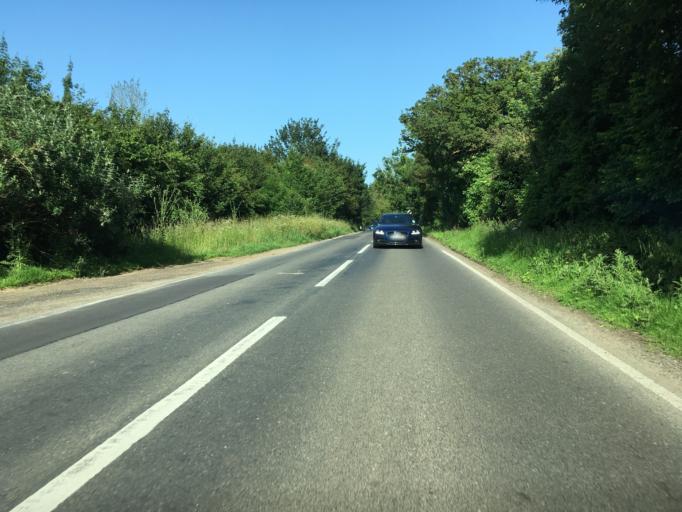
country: GB
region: England
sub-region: Oxfordshire
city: Charlbury
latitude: 51.9227
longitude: -1.4438
